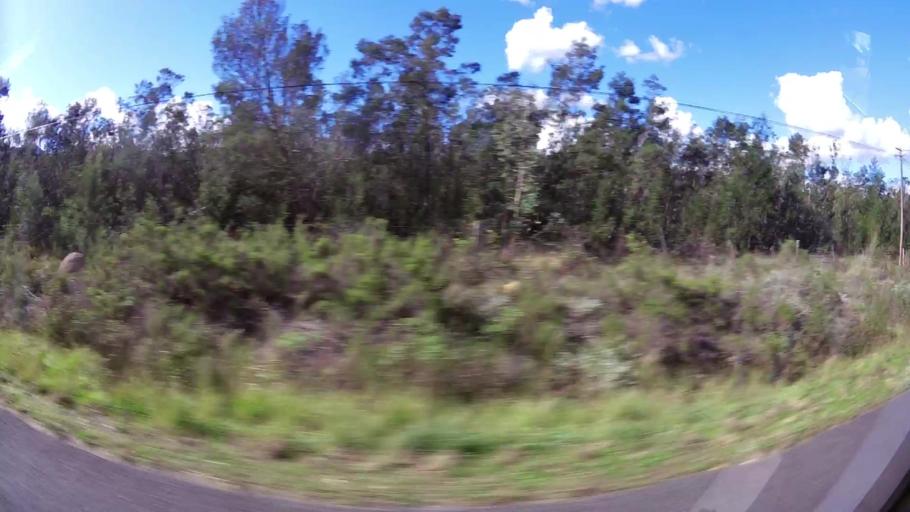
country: ZA
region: Western Cape
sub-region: Overberg District Municipality
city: Swellendam
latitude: -34.0314
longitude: 20.4204
